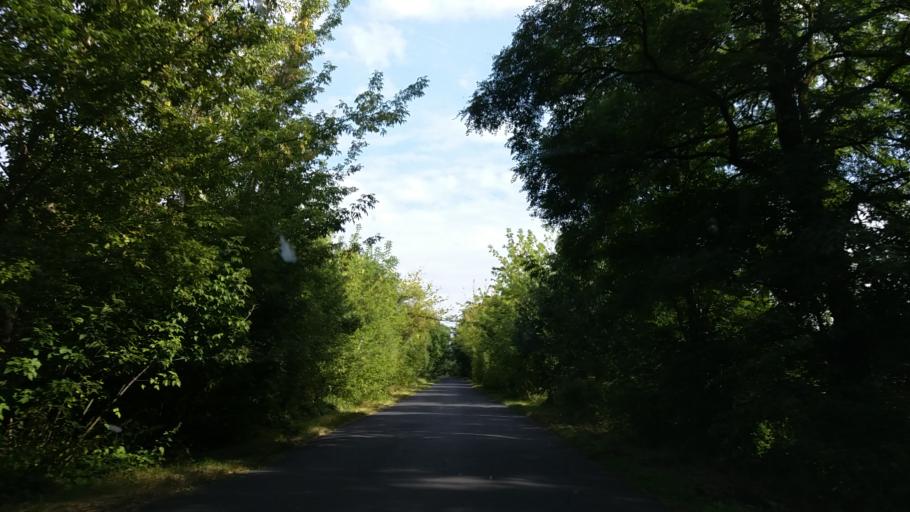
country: PL
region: West Pomeranian Voivodeship
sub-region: Powiat stargardzki
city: Suchan
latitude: 53.2253
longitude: 15.2811
